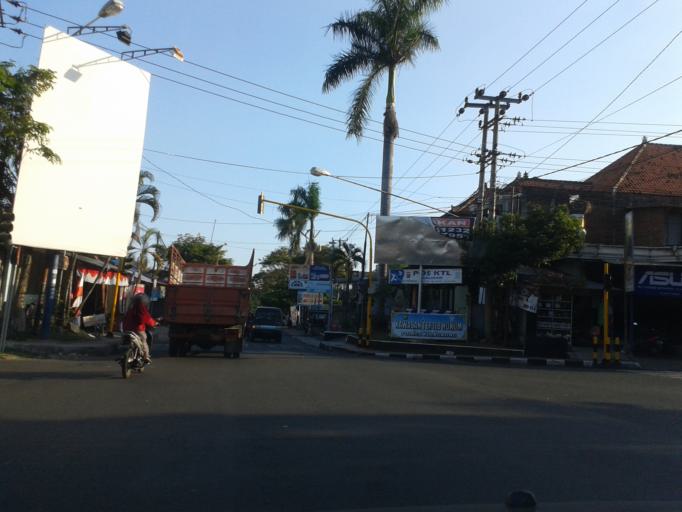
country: ID
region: Bali
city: Semarapura
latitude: -8.5423
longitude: 115.4027
